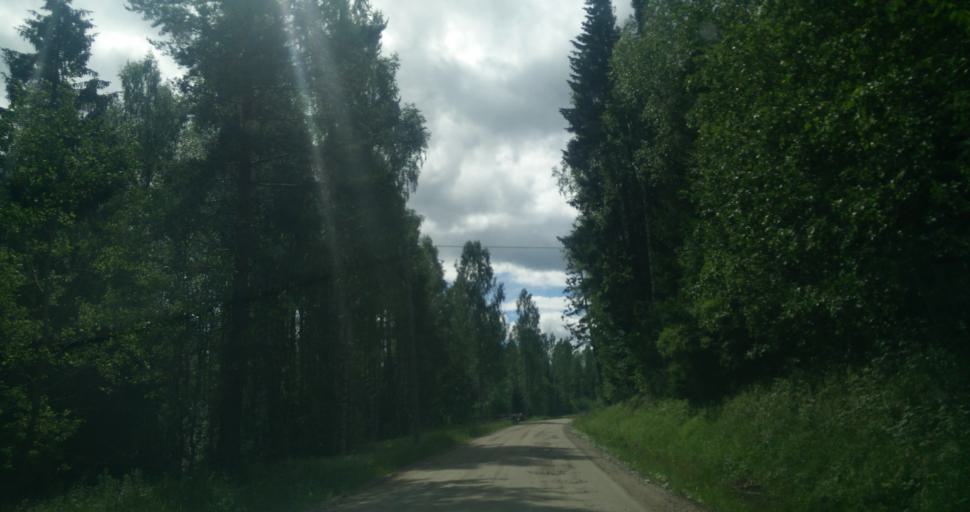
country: SE
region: Gaevleborg
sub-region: Nordanstigs Kommun
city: Bergsjoe
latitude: 62.1296
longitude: 17.1258
